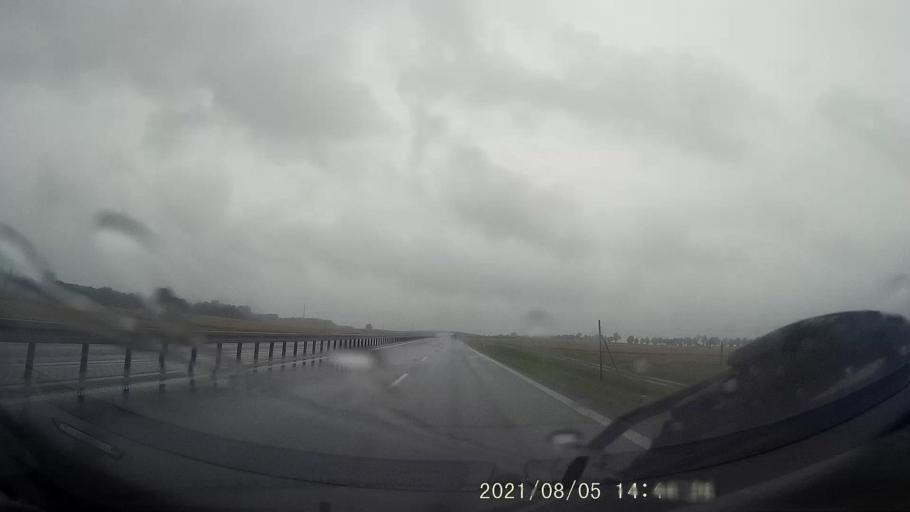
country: PL
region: Opole Voivodeship
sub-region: Powiat nyski
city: Nysa
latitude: 50.4940
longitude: 17.3785
